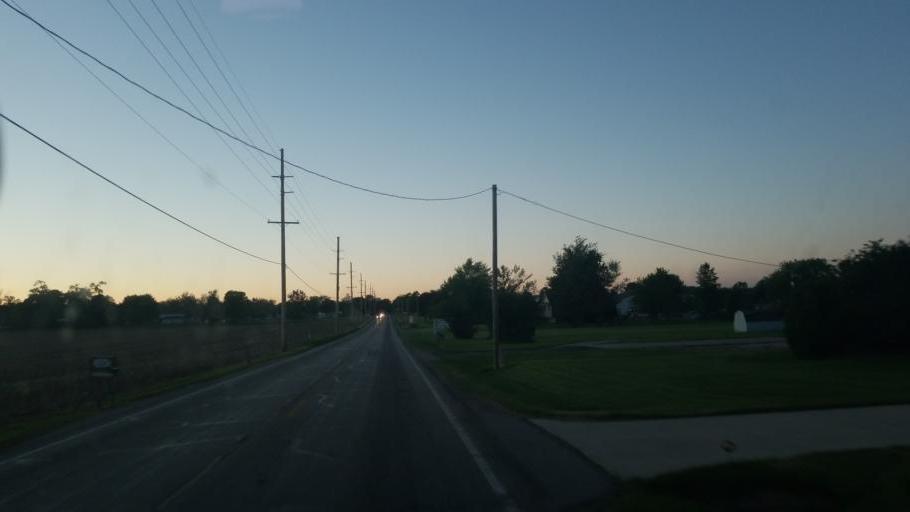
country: US
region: Indiana
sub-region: Elkhart County
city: Nappanee
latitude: 41.4305
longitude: -86.0013
